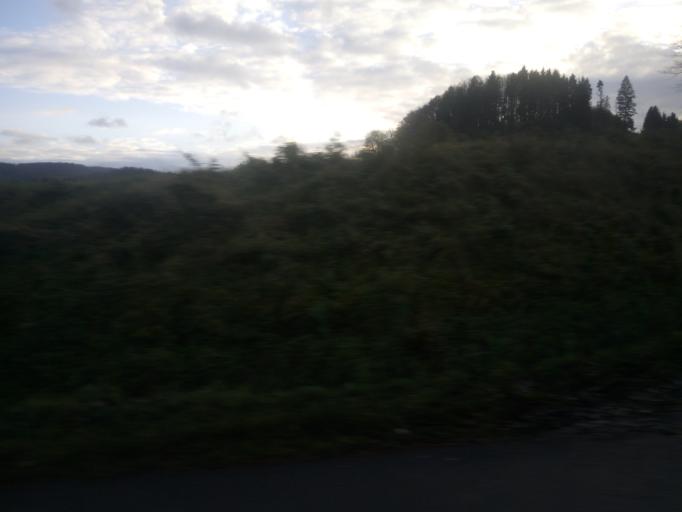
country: LU
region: Diekirch
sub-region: Canton de Vianden
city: Vianden
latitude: 49.9149
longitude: 6.2161
